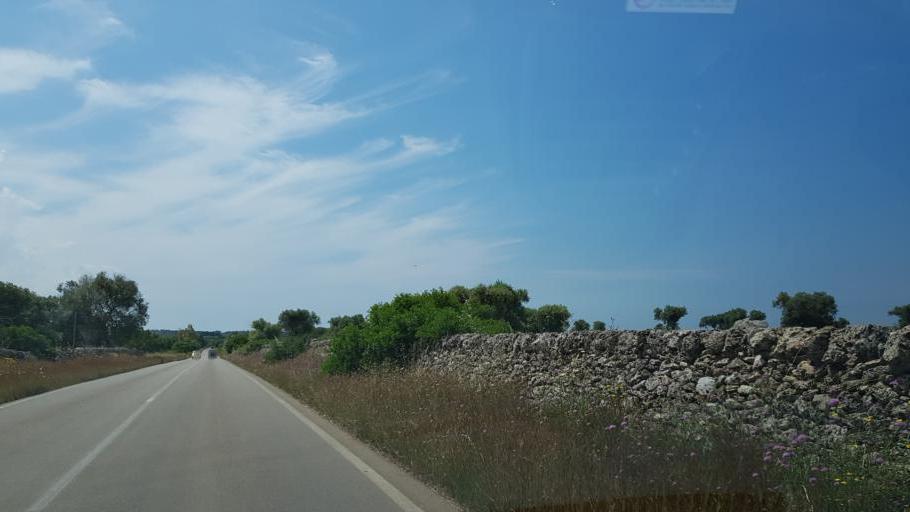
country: IT
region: Apulia
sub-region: Provincia di Lecce
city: Porto Cesareo
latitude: 40.3162
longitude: 17.8610
